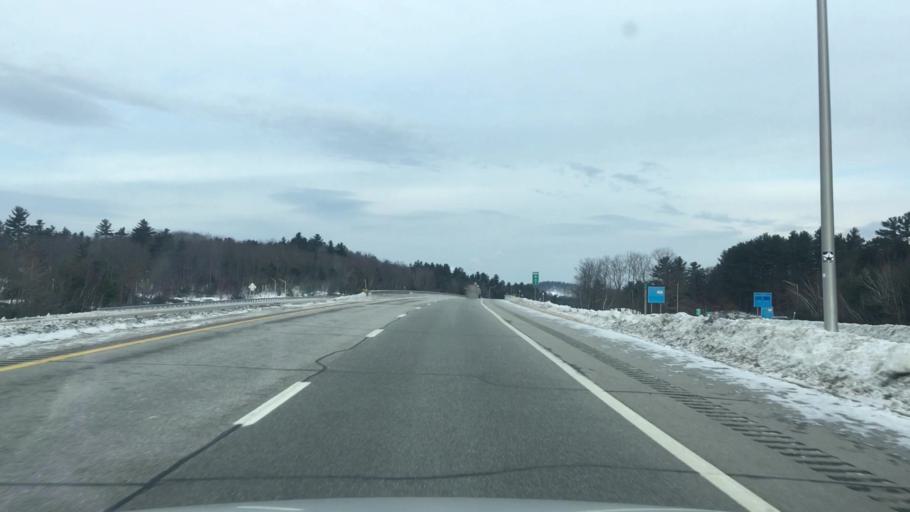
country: US
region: New Hampshire
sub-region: Merrimack County
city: New London
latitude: 43.4205
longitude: -72.0356
